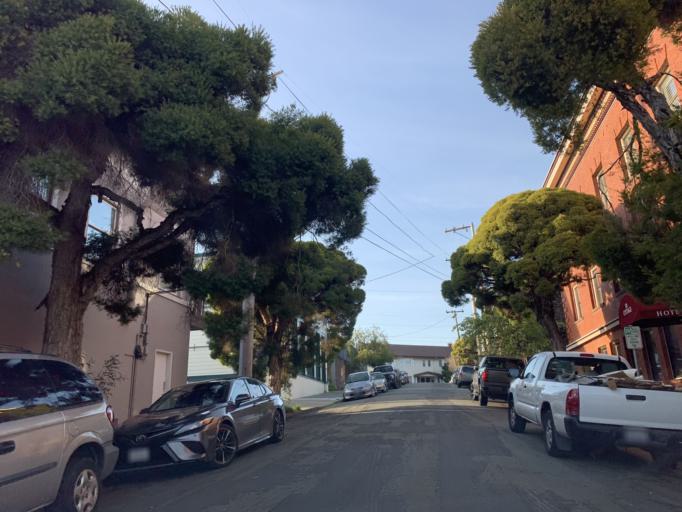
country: US
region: California
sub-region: Contra Costa County
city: North Richmond
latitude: 37.9272
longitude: -122.3848
